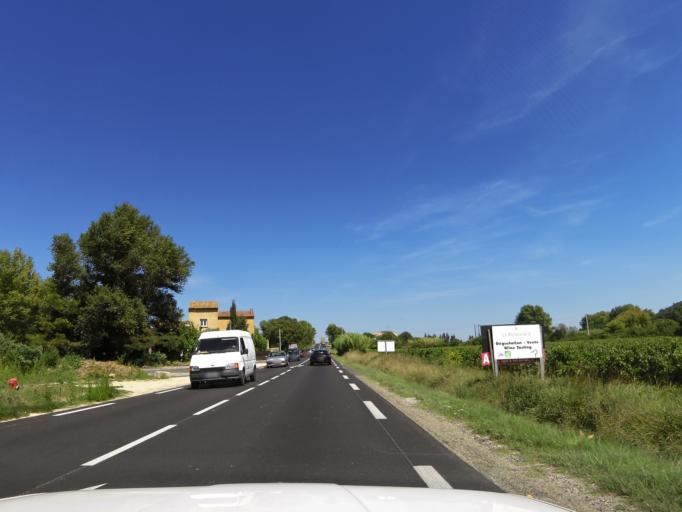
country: FR
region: Languedoc-Roussillon
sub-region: Departement du Gard
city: Saint-Nazaire
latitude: 44.1834
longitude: 4.6209
